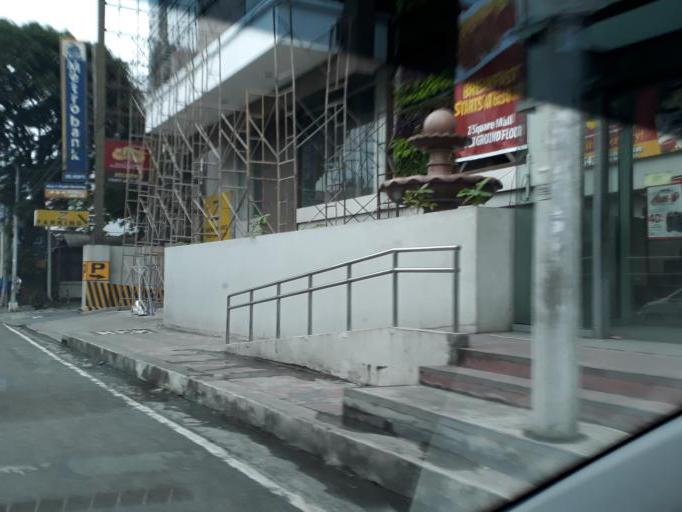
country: PH
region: Calabarzon
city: Del Monte
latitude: 14.6385
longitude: 121.0007
